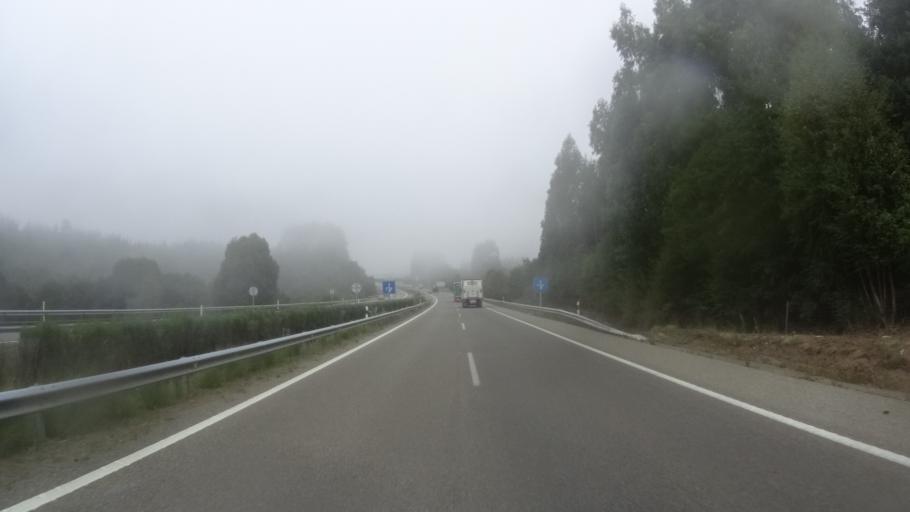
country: ES
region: Galicia
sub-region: Provincia de Lugo
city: Guitiriz
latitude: 43.1812
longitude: -7.8130
